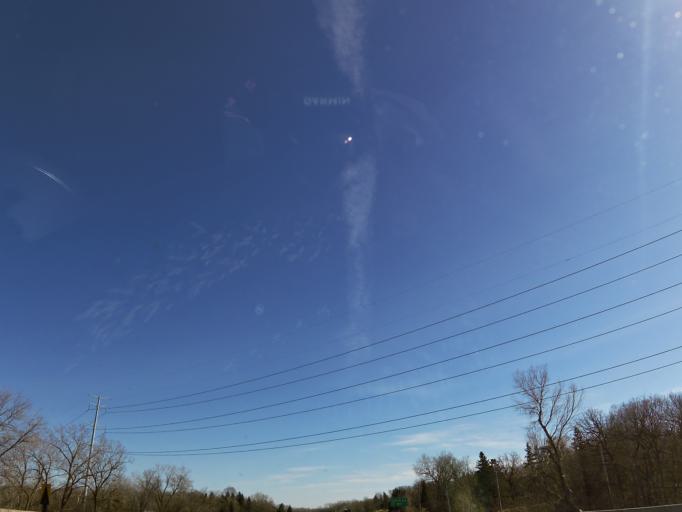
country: US
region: Minnesota
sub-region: Hennepin County
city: Plymouth
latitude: 44.9964
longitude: -93.4390
